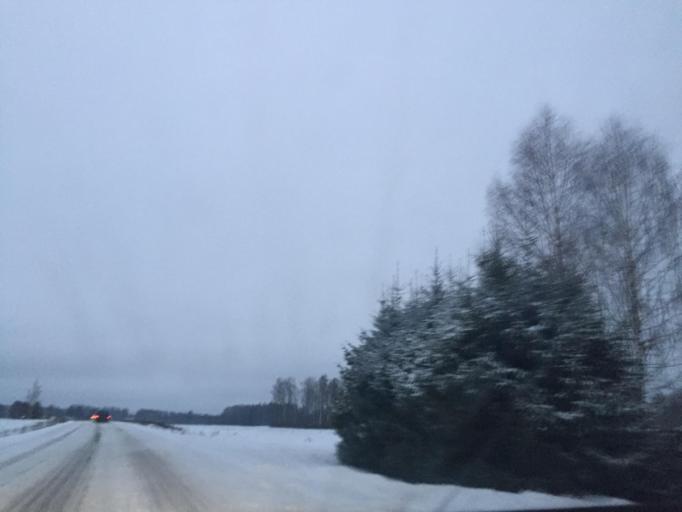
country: LV
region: Raunas
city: Rauna
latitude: 57.4282
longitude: 25.5997
